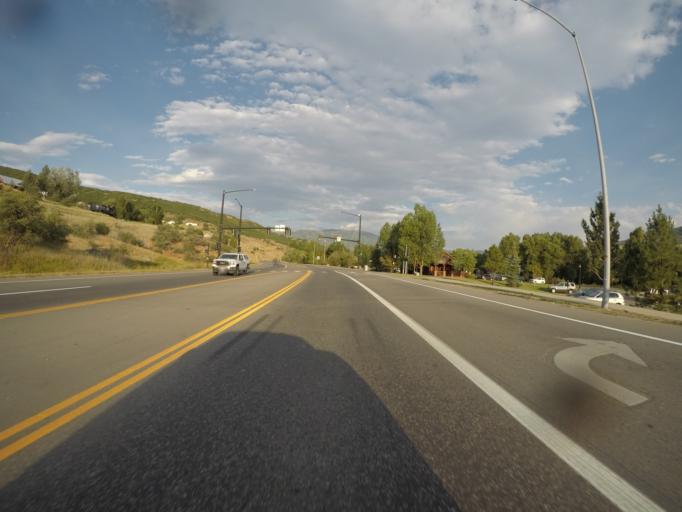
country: US
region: Colorado
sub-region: Routt County
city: Steamboat Springs
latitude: 40.4945
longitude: -106.8507
